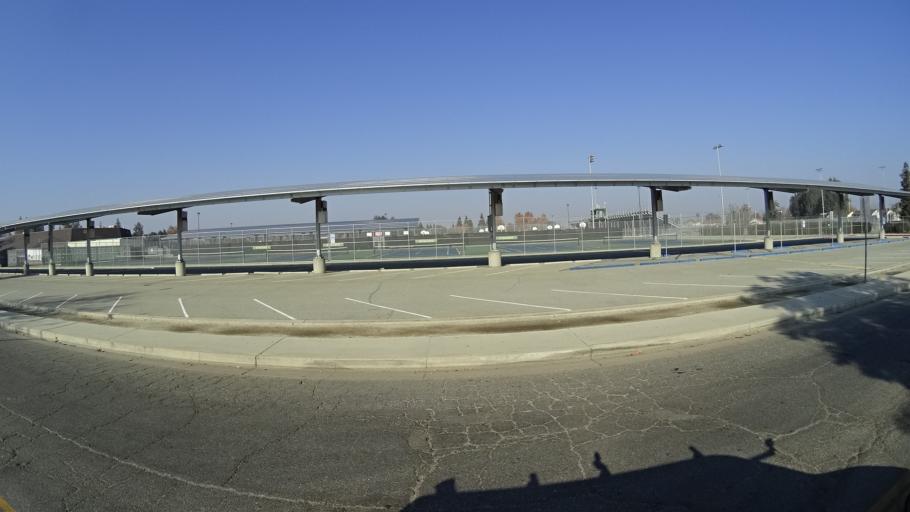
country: US
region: California
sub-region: Kern County
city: Bakersfield
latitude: 35.3419
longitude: -119.0570
